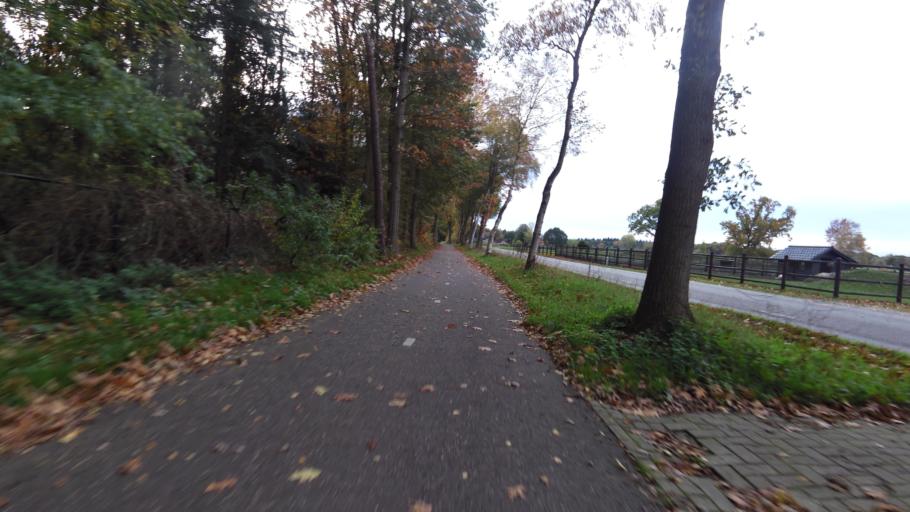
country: NL
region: Gelderland
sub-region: Gemeente Oldebroek
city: Oldebroek
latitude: 52.4251
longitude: 5.9122
